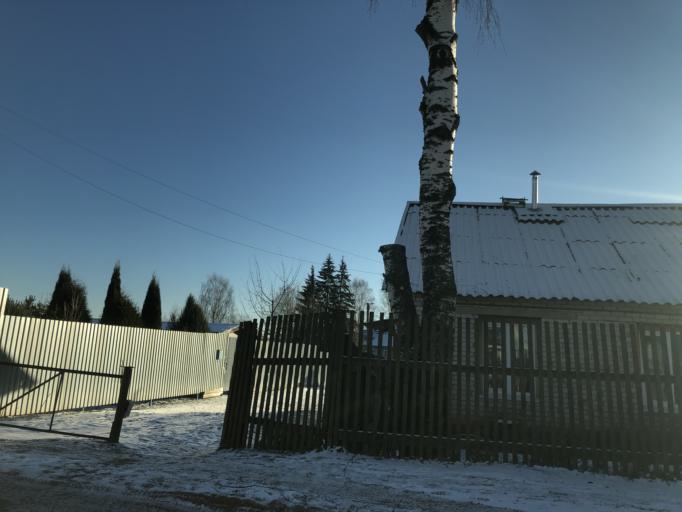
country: RU
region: Tverskaya
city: Rzhev
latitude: 56.2826
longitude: 34.3213
